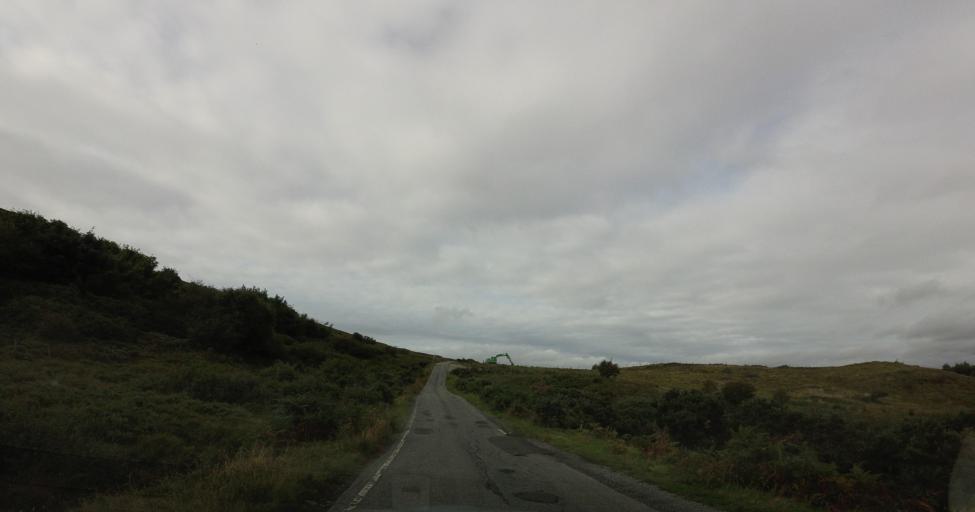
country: GB
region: Scotland
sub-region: Highland
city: Portree
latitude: 57.4212
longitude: -6.2488
